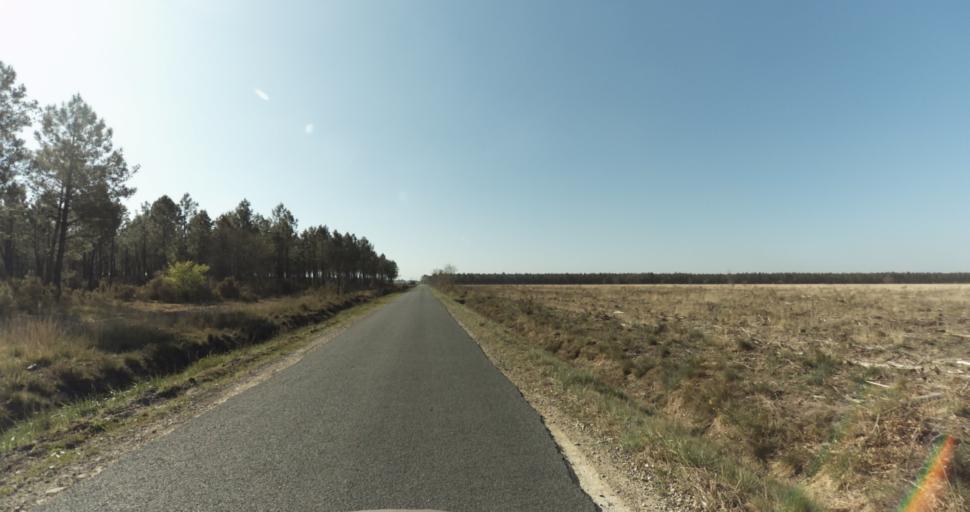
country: FR
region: Aquitaine
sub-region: Departement de la Gironde
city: Marcheprime
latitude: 44.7807
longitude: -0.8606
